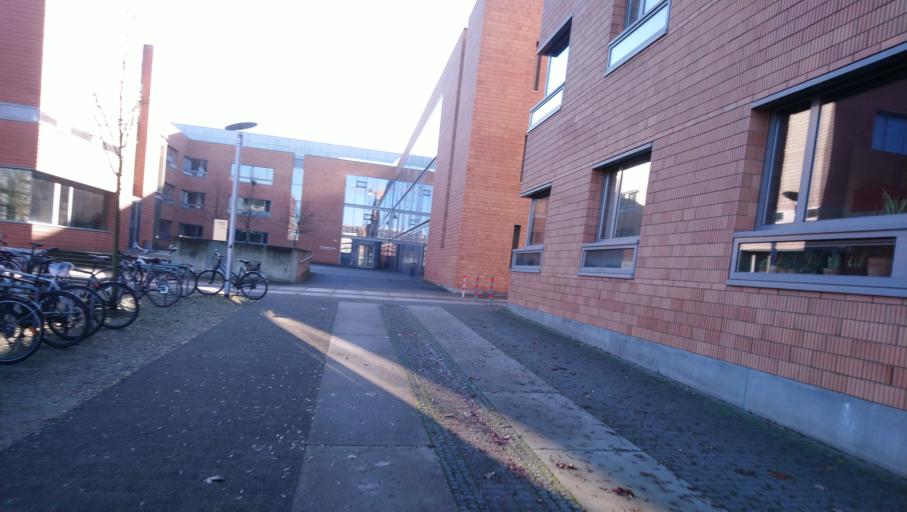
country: DE
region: Mecklenburg-Vorpommern
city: Rostock
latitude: 54.0772
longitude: 12.1126
